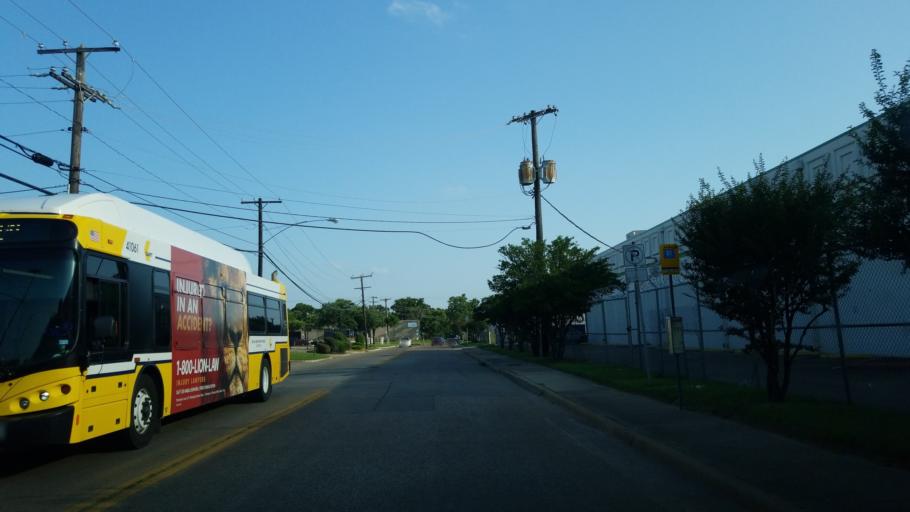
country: US
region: Texas
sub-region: Dallas County
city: Farmers Branch
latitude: 32.8755
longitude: -96.8903
